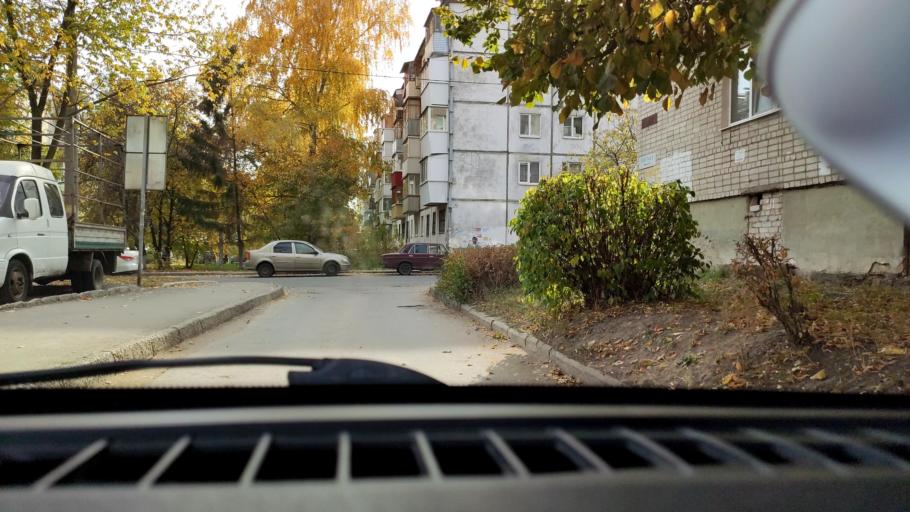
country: RU
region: Samara
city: Petra-Dubrava
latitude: 53.2989
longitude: 50.2806
